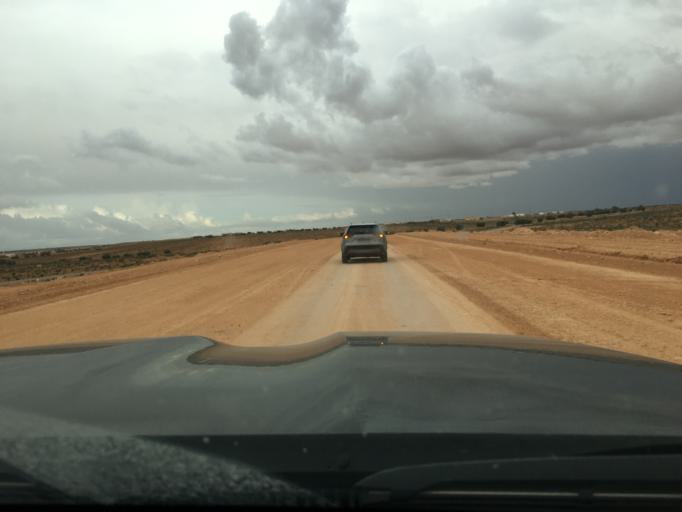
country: TN
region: Madanin
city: Medenine
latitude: 33.2856
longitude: 10.5992
